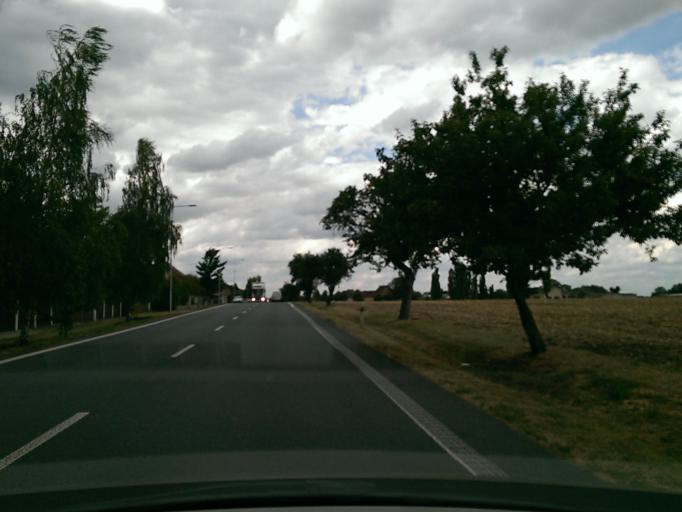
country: CZ
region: Central Bohemia
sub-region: Okres Nymburk
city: Nymburk
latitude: 50.2154
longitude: 15.0310
